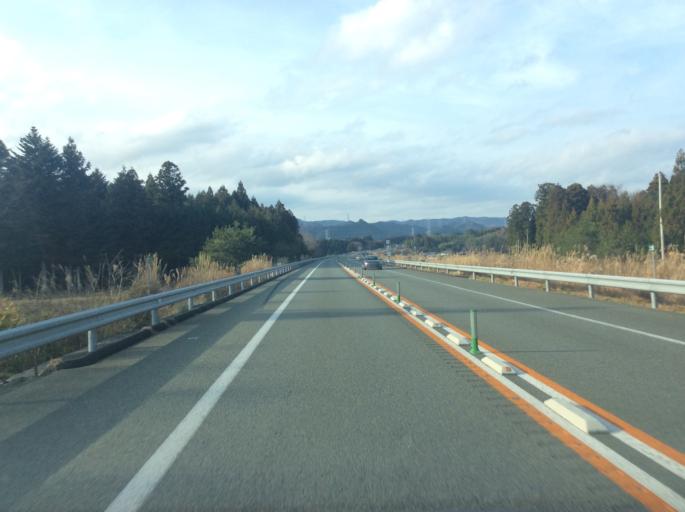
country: JP
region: Fukushima
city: Namie
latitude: 37.3517
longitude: 140.9806
